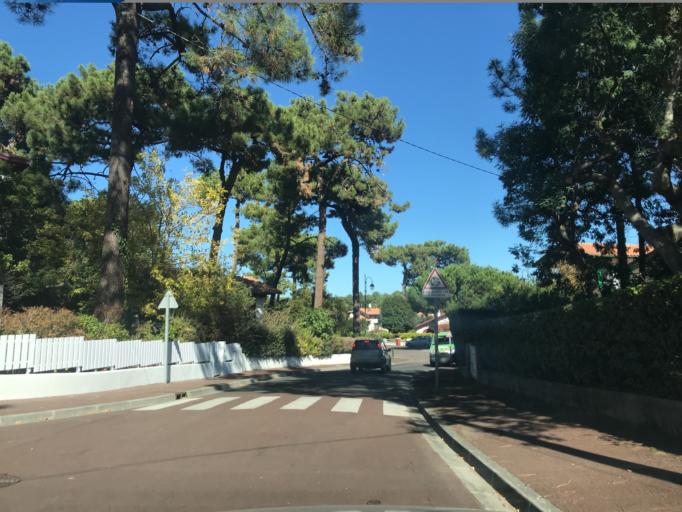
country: FR
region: Aquitaine
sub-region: Departement de la Gironde
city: Arcachon
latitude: 44.6493
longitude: -1.1800
